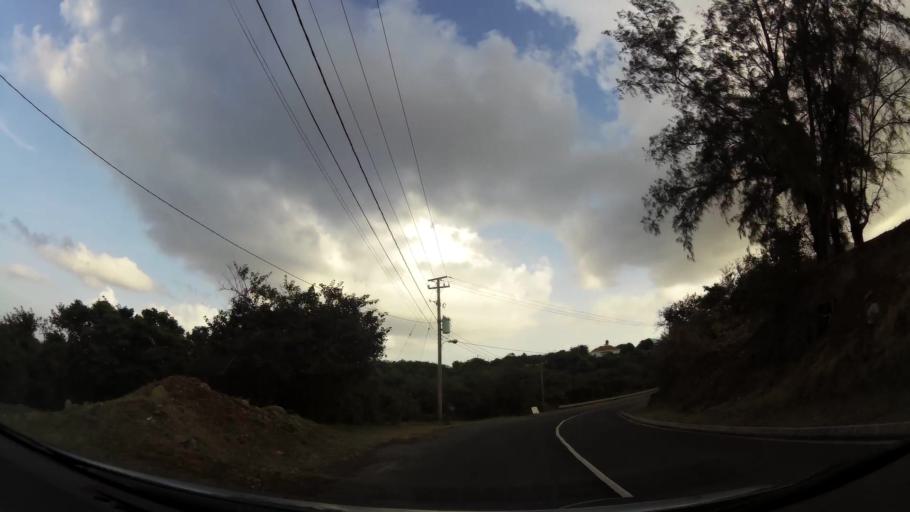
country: KN
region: Saint James Windwa
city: Newcastle
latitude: 17.1893
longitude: -62.5612
